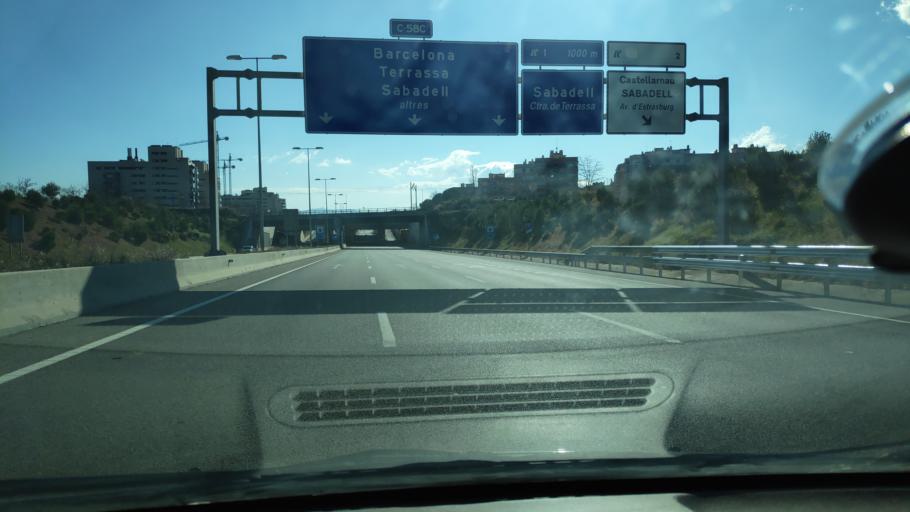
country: ES
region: Catalonia
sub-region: Provincia de Barcelona
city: Sant Quirze del Valles
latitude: 41.5653
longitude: 2.0769
